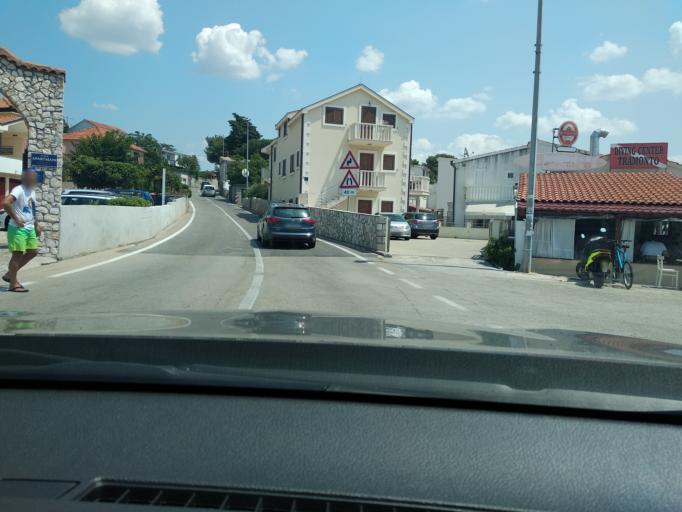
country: HR
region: Sibensko-Kniniska
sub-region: Grad Sibenik
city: Tisno
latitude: 43.7993
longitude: 15.6446
